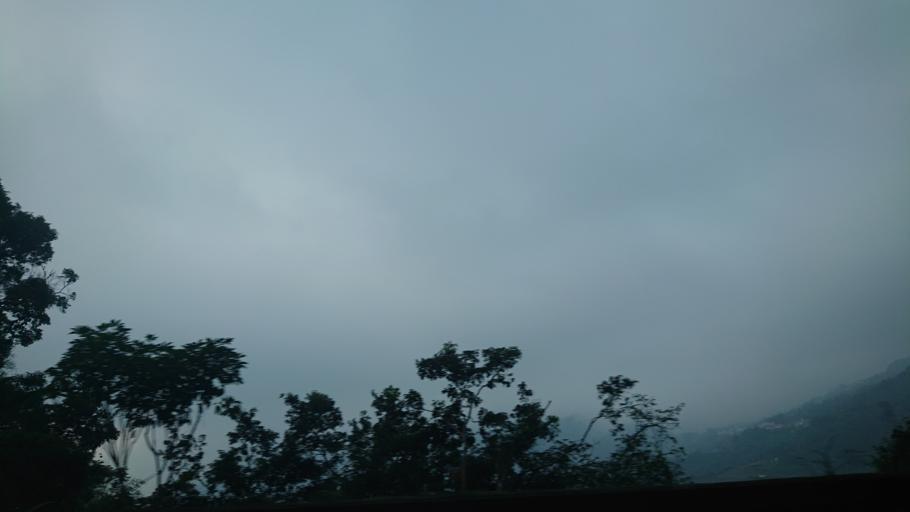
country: TW
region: Taiwan
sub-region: Chiayi
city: Jiayi Shi
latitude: 23.4642
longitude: 120.7186
